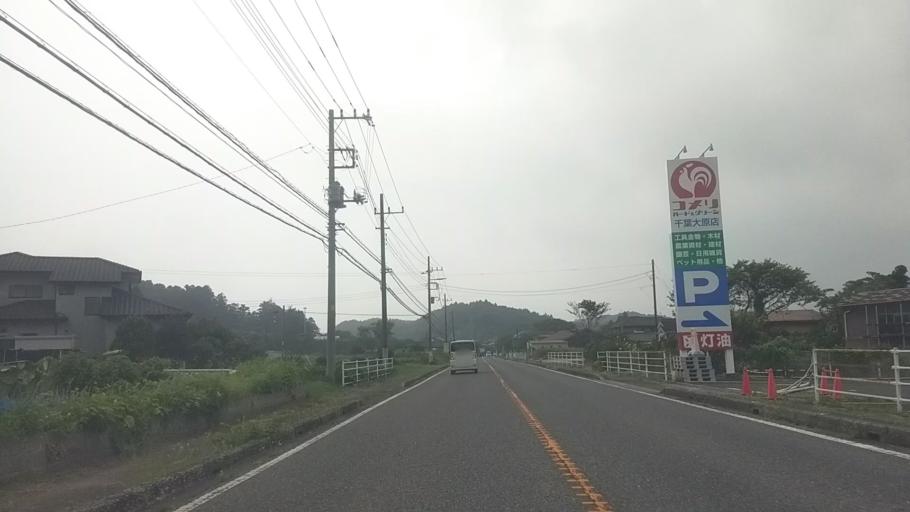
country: JP
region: Chiba
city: Ohara
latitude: 35.2269
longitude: 140.3869
